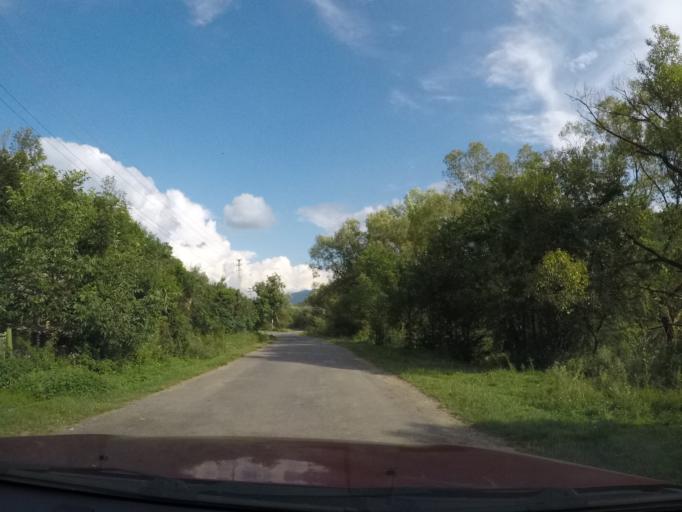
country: UA
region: Zakarpattia
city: Velykyi Bereznyi
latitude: 49.0138
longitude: 22.6223
